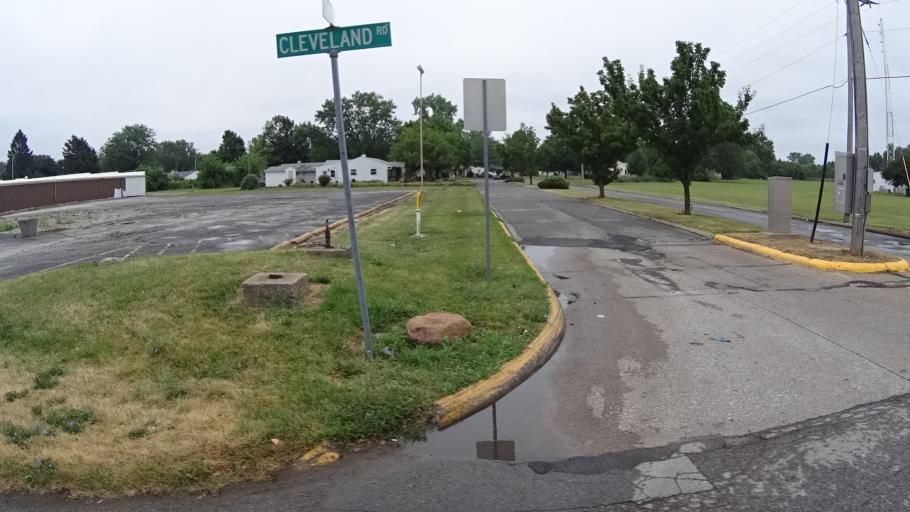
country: US
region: Ohio
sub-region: Erie County
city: Sandusky
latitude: 41.4423
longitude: -82.6852
